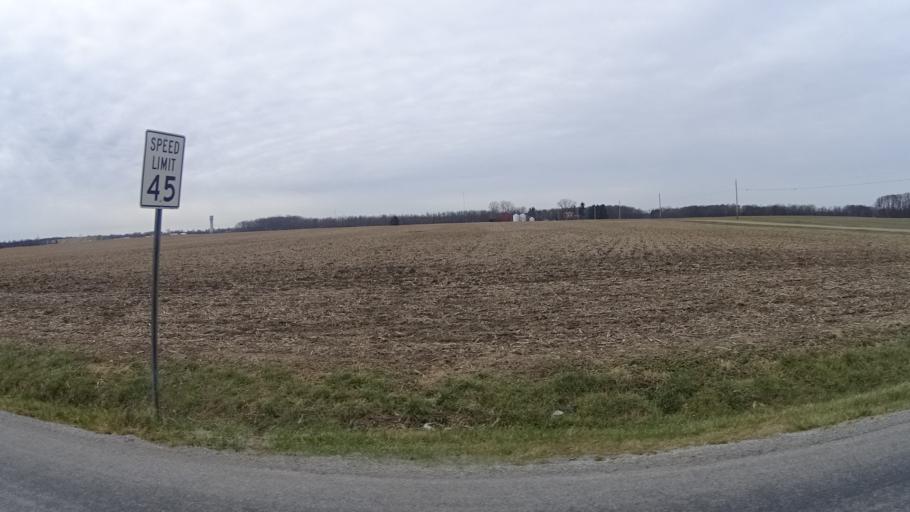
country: US
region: Ohio
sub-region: Lorain County
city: Wellington
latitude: 41.1887
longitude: -82.1930
